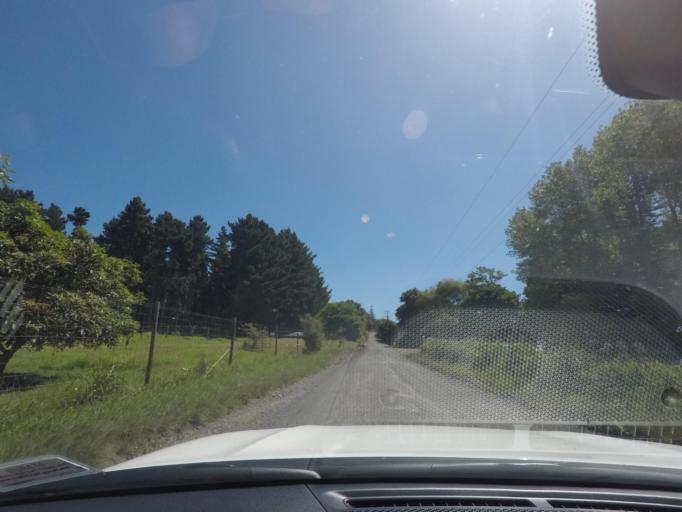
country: NZ
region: Auckland
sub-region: Auckland
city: Parakai
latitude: -36.5802
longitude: 174.3197
